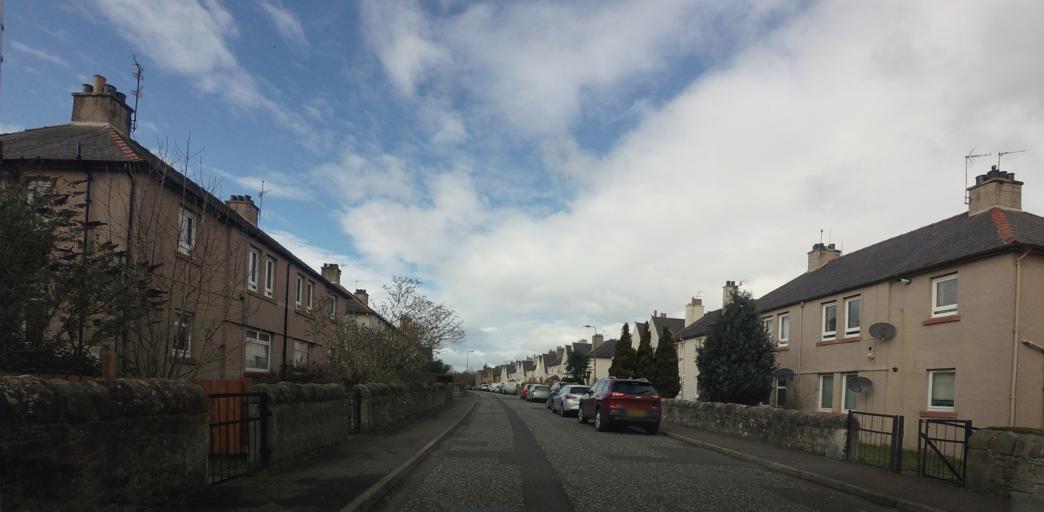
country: GB
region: Scotland
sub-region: Edinburgh
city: Queensferry
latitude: 55.9907
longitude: -3.4067
